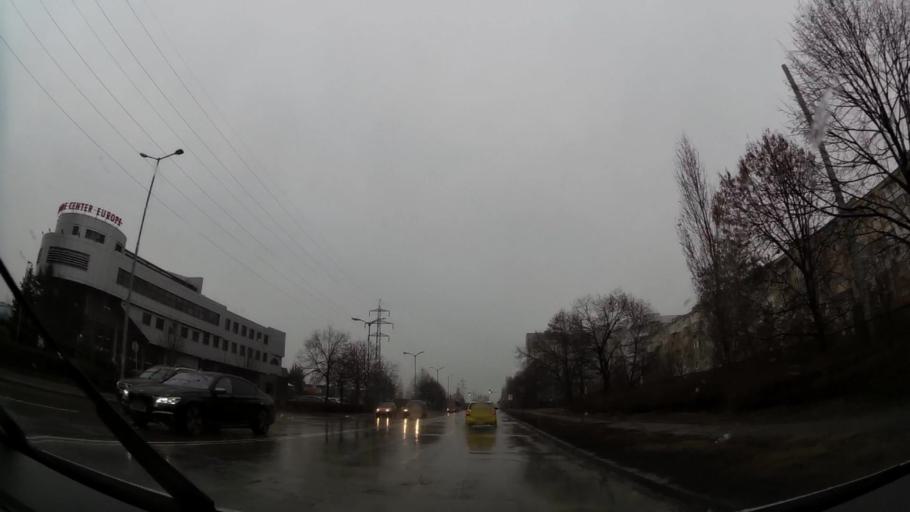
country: BG
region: Sofia-Capital
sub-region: Stolichna Obshtina
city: Sofia
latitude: 42.6712
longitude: 23.3961
